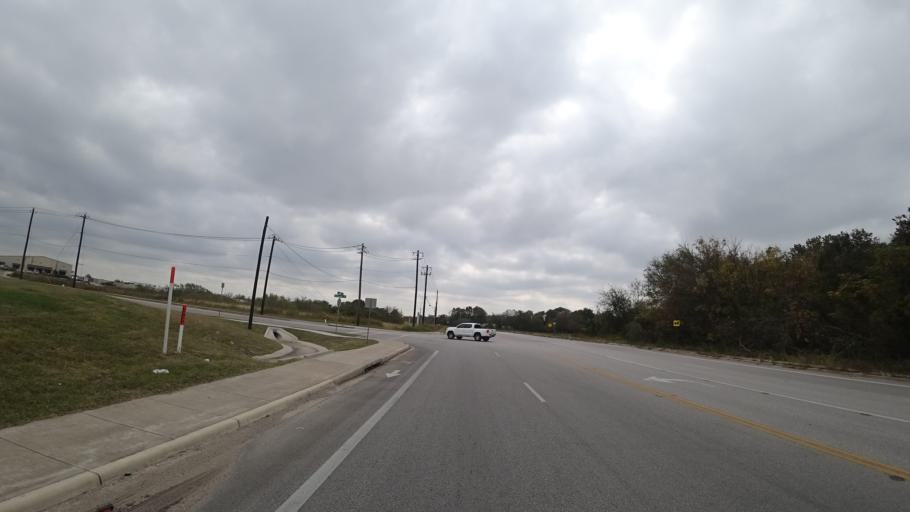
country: US
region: Texas
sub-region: Travis County
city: Pflugerville
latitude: 30.3994
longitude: -97.6333
